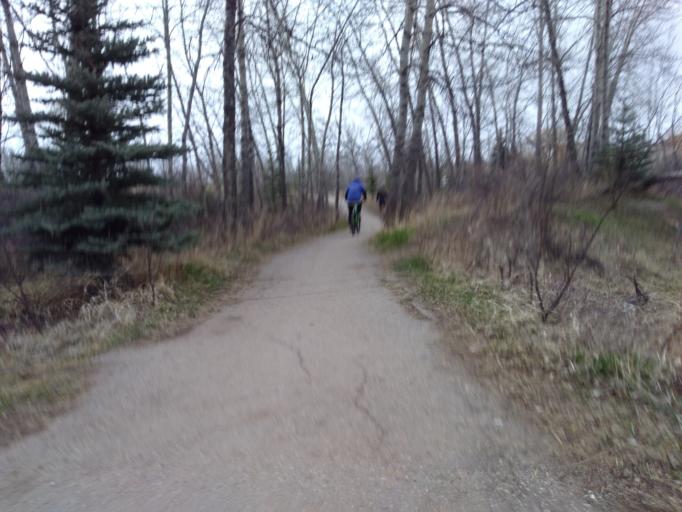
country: CA
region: Alberta
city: Cochrane
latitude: 51.1885
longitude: -114.4805
